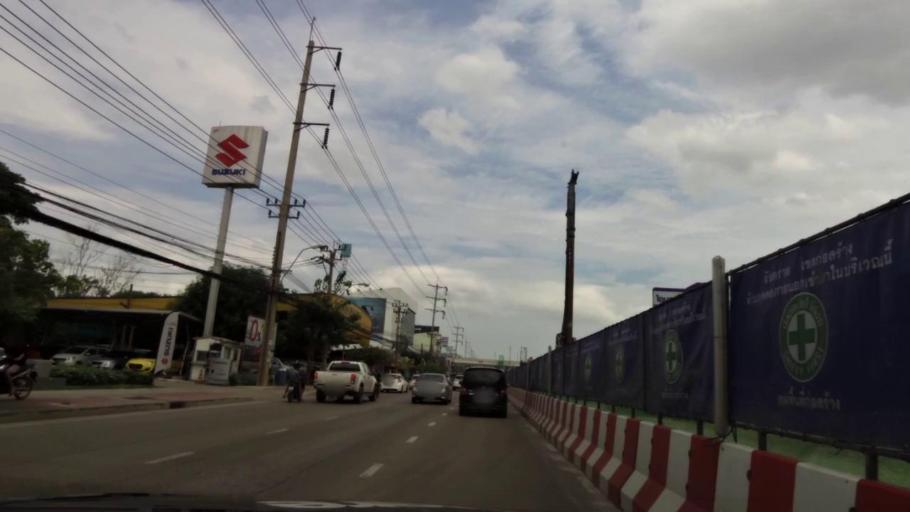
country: TH
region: Bangkok
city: Suan Luang
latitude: 13.7014
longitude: 100.6464
